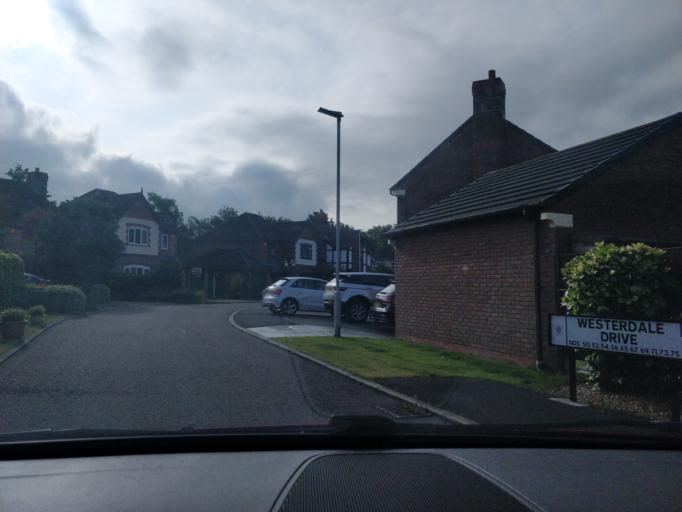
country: GB
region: England
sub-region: Lancashire
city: Banks
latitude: 53.6742
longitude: -2.9127
